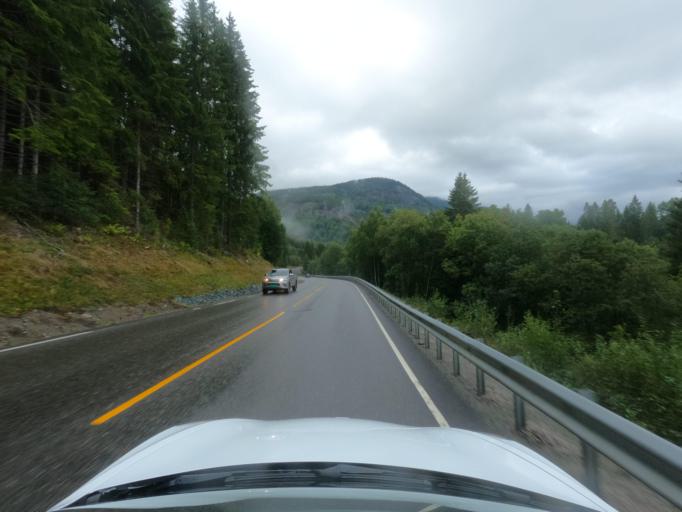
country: NO
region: Telemark
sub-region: Seljord
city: Seljord
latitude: 59.4520
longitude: 8.5616
